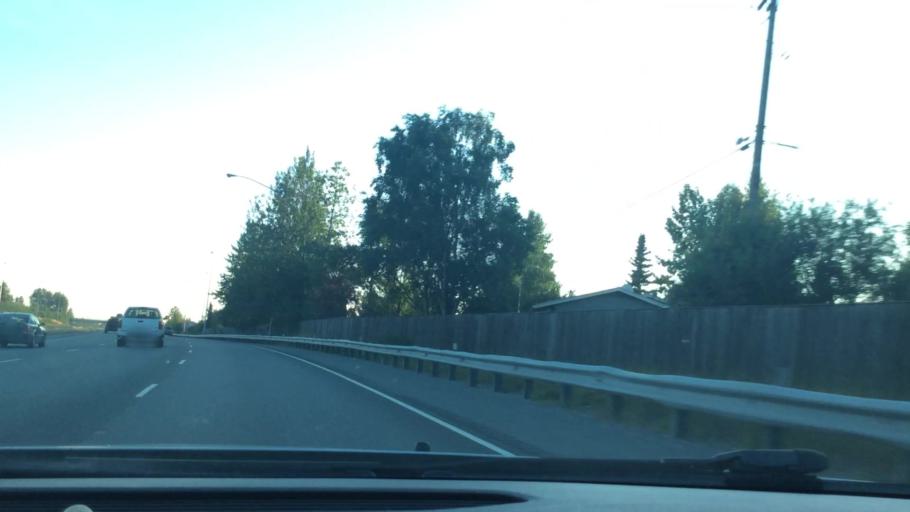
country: US
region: Alaska
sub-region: Anchorage Municipality
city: Anchorage
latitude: 61.2244
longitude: -149.7937
